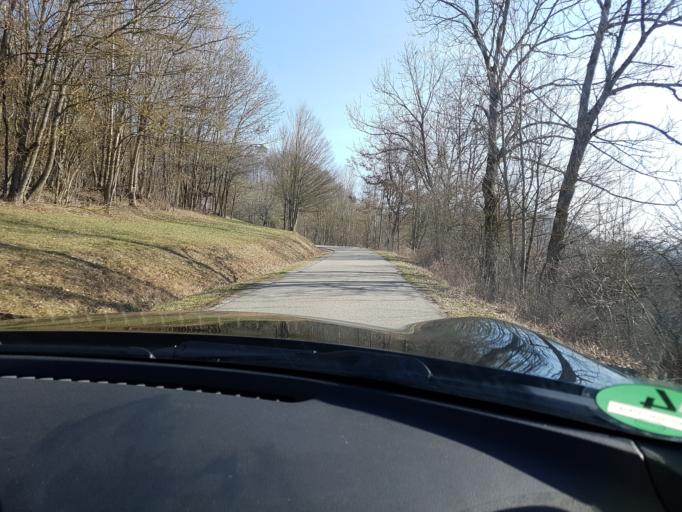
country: DE
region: Baden-Wuerttemberg
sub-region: Regierungsbezirk Stuttgart
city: Langenburg
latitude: 49.2930
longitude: 9.8384
